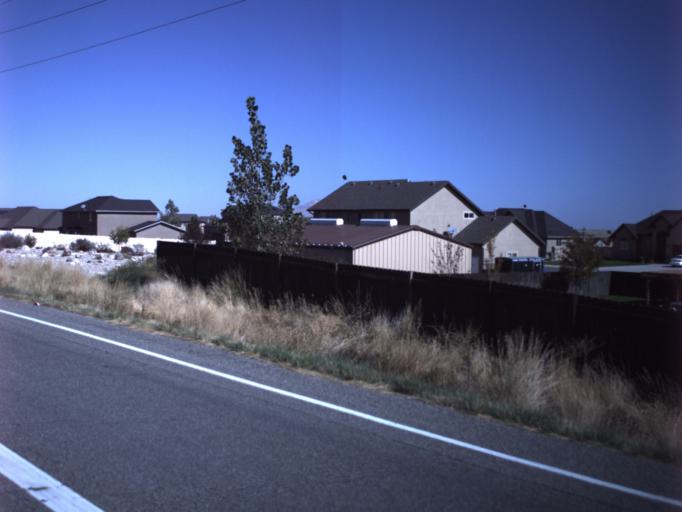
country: US
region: Utah
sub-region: Tooele County
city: Grantsville
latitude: 40.6188
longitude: -112.5012
